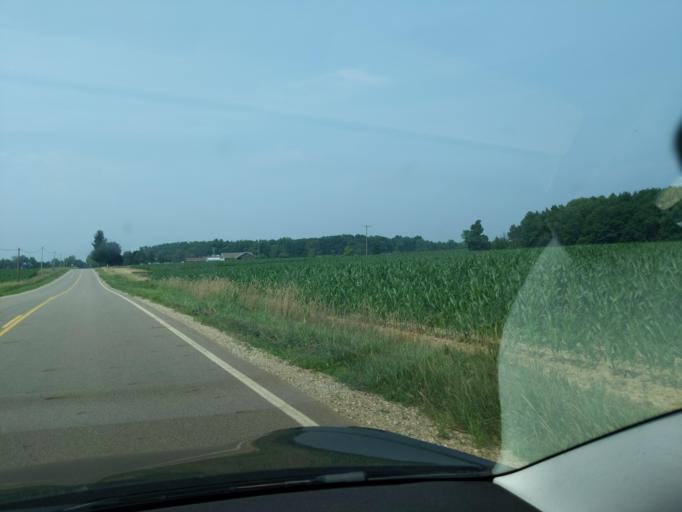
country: US
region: Michigan
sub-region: Clinton County
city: DeWitt
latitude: 42.8618
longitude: -84.5723
